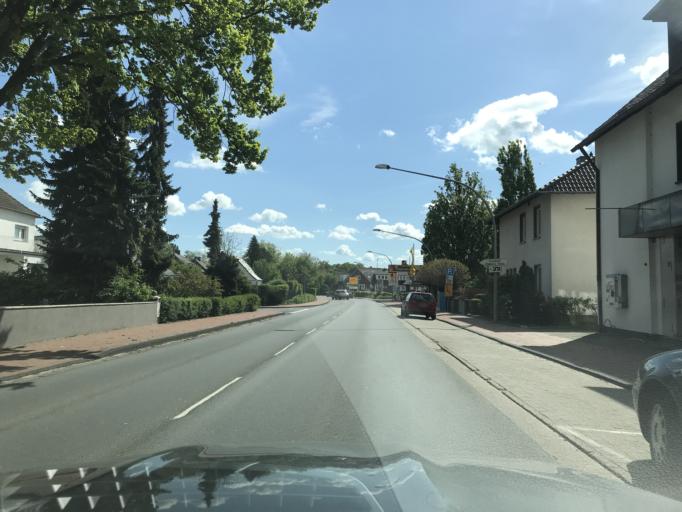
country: DE
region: North Rhine-Westphalia
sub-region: Regierungsbezirk Munster
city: Westerkappeln
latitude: 52.3130
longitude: 7.8807
